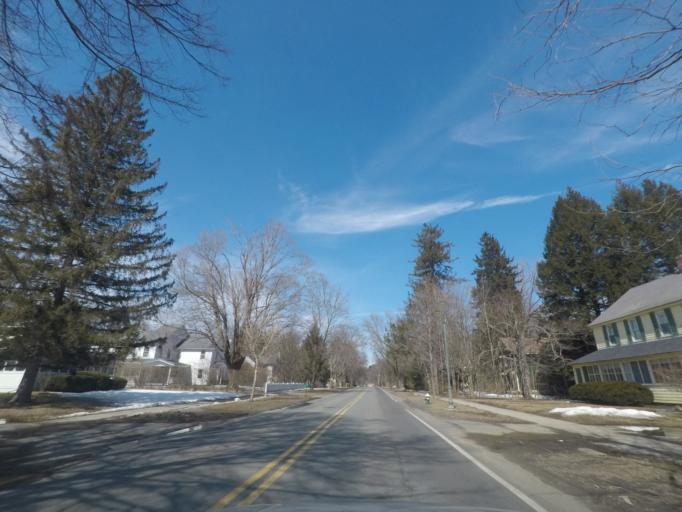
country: US
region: Massachusetts
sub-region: Berkshire County
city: Stockbridge
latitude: 42.2879
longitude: -73.3207
